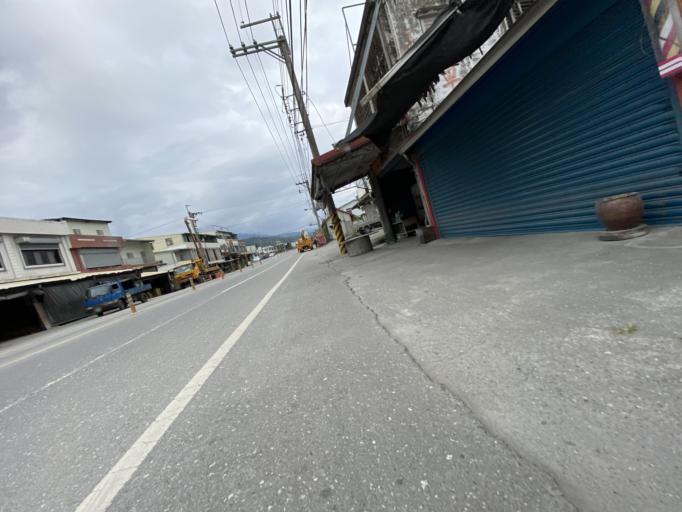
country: TW
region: Taiwan
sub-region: Taitung
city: Taitung
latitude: 23.3821
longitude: 121.3299
